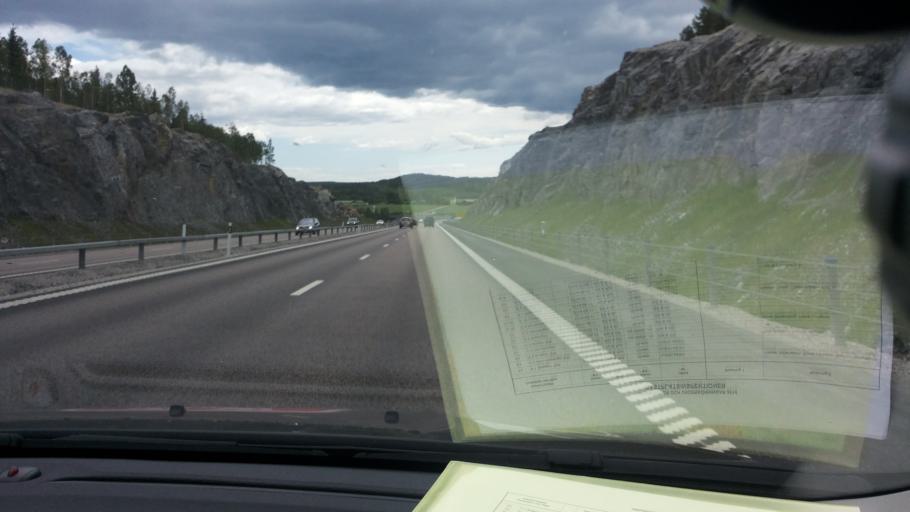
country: SE
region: Vaesternorrland
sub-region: Sundsvalls Kommun
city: Nolby
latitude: 62.3017
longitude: 17.3450
